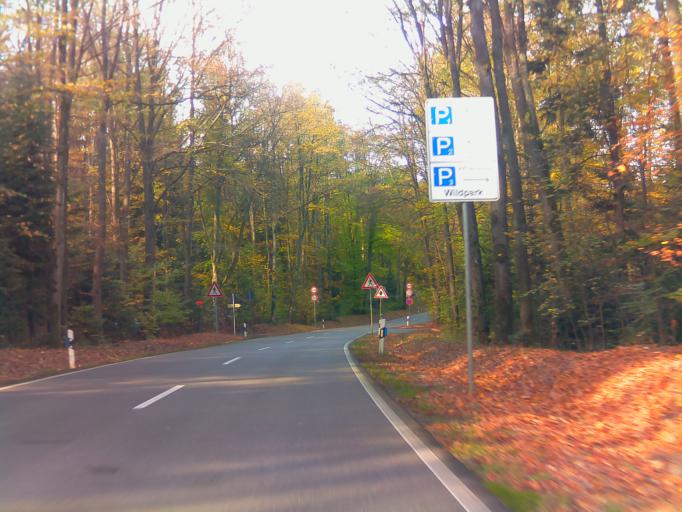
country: DE
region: Baden-Wuerttemberg
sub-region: Karlsruhe Region
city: Pforzheim
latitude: 48.8739
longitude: 8.7209
